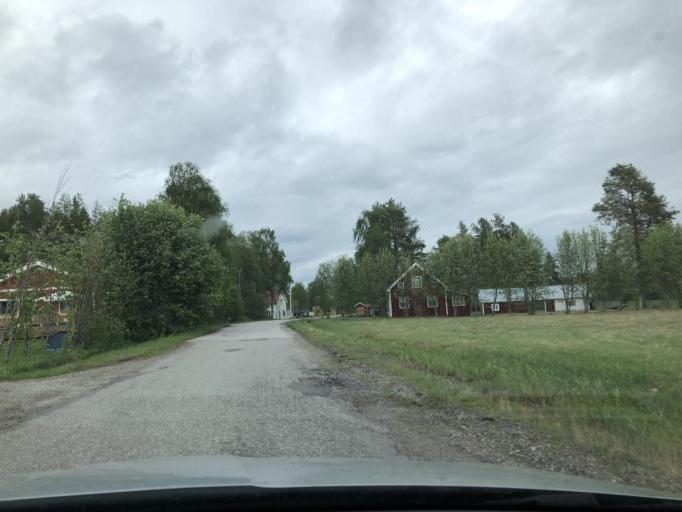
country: SE
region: Norrbotten
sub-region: Pitea Kommun
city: Roknas
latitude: 65.3742
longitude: 21.2773
